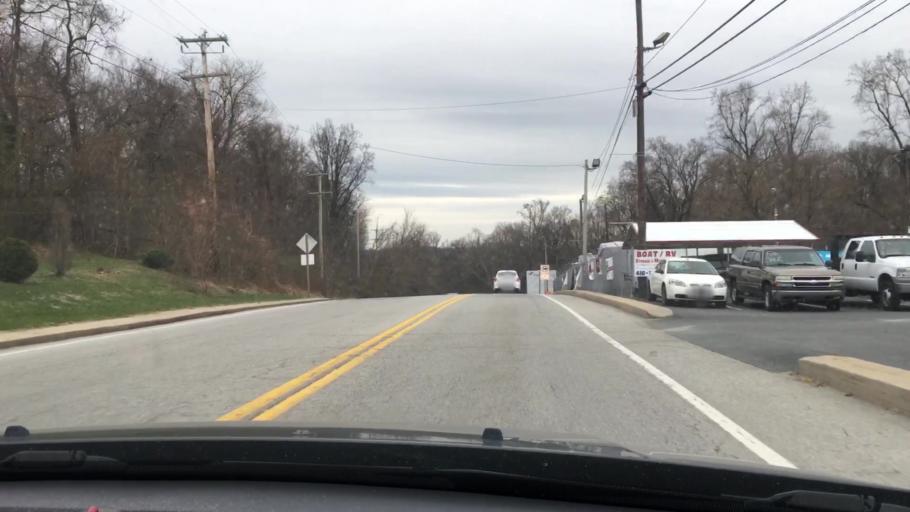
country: US
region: Maryland
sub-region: Cecil County
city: Rising Sun
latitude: 39.6734
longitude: -76.1670
